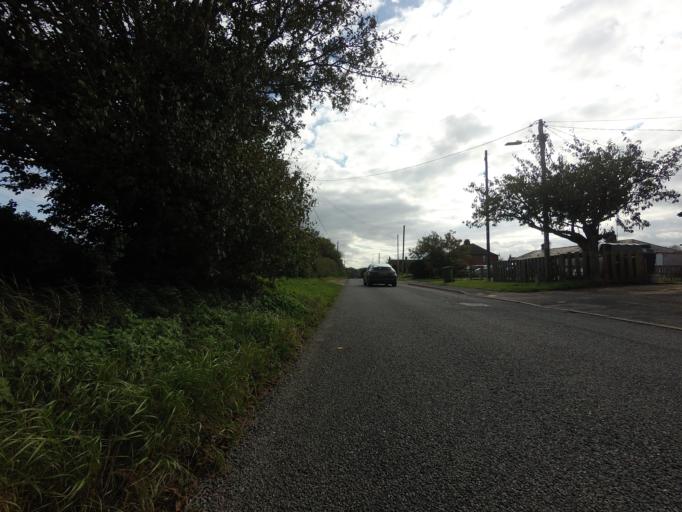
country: GB
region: England
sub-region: Norfolk
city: Snettisham
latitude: 52.9027
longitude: 0.5437
